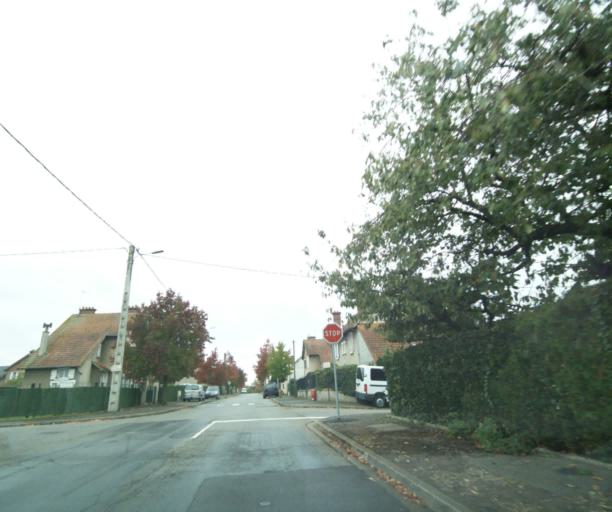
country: FR
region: Centre
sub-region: Departement d'Eure-et-Loir
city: Dreux
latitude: 48.7297
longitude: 1.3720
